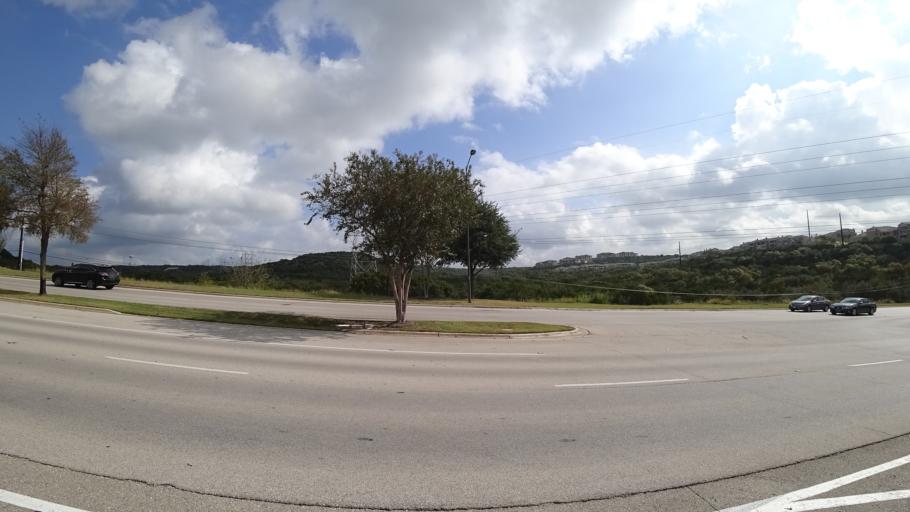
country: US
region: Texas
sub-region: Travis County
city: Hudson Bend
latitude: 30.3877
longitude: -97.8825
